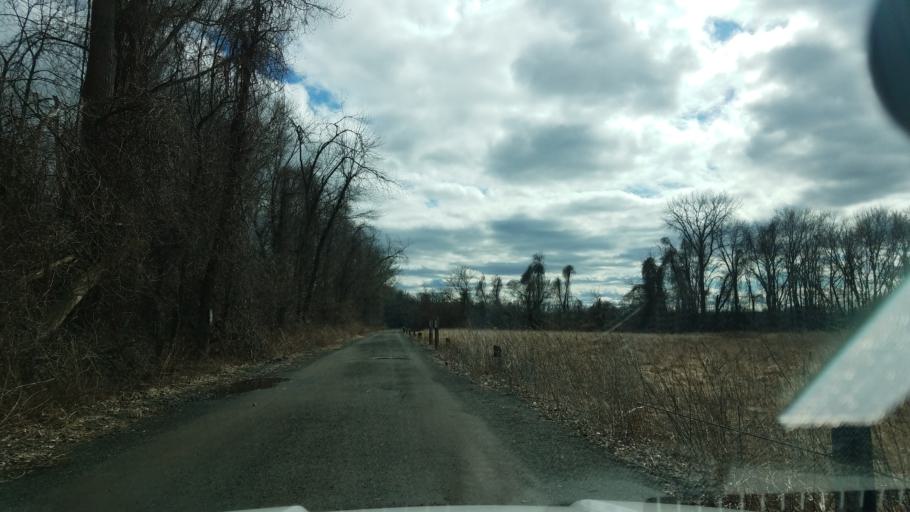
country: US
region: Connecticut
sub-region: Hartford County
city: Wethersfield
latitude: 41.7086
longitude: -72.6366
